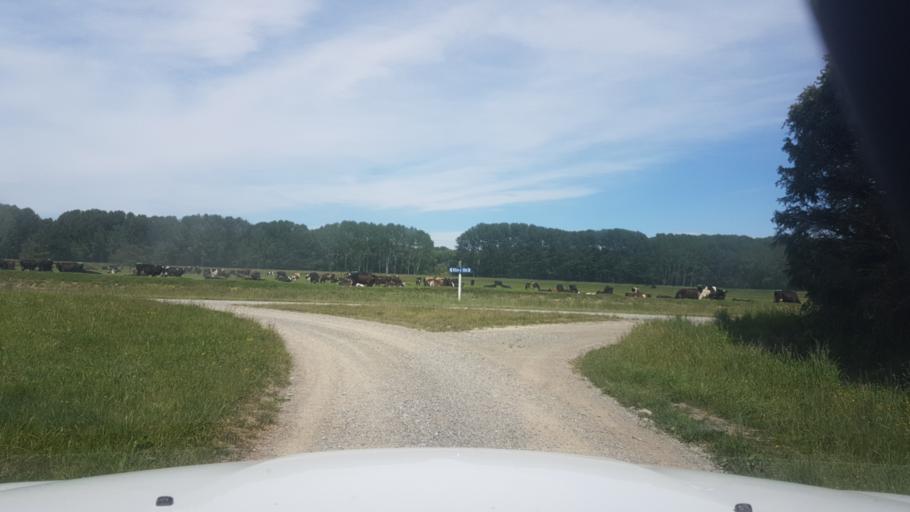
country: NZ
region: Canterbury
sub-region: Timaru District
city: Pleasant Point
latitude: -44.2231
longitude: 171.1193
